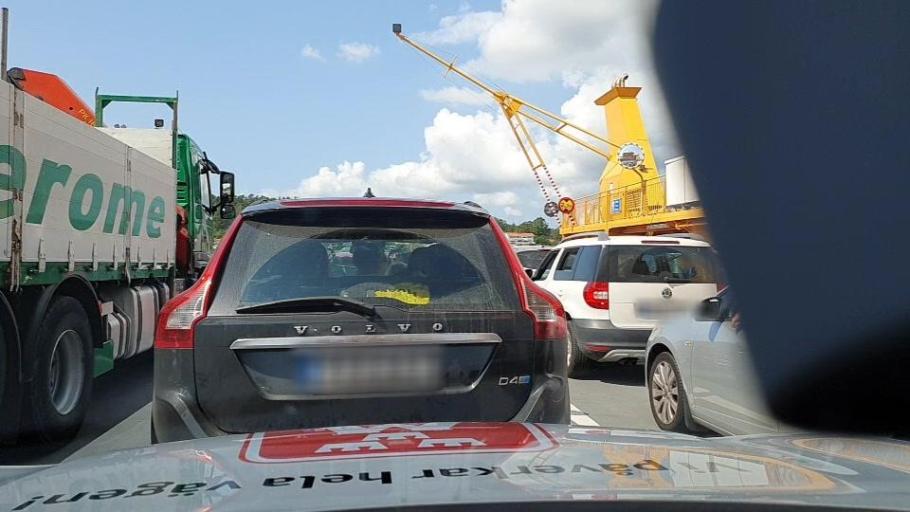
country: SE
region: Vaestra Goetaland
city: Svanesund
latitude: 58.1358
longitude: 11.8381
